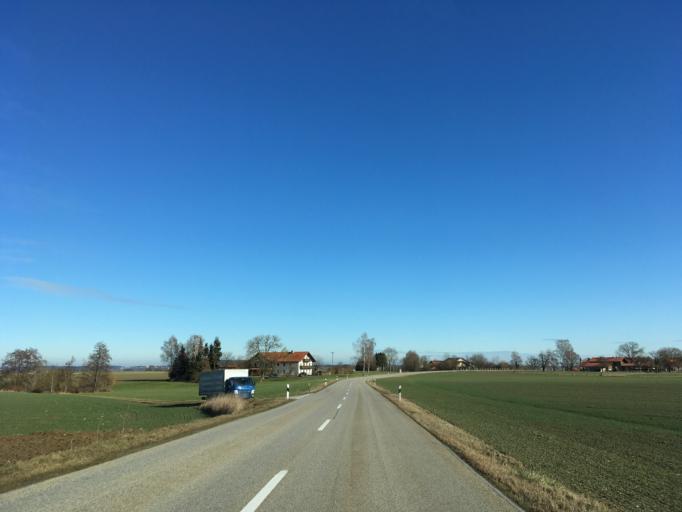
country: DE
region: Bavaria
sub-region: Upper Bavaria
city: Obertaufkirchen
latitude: 48.2407
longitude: 12.2771
